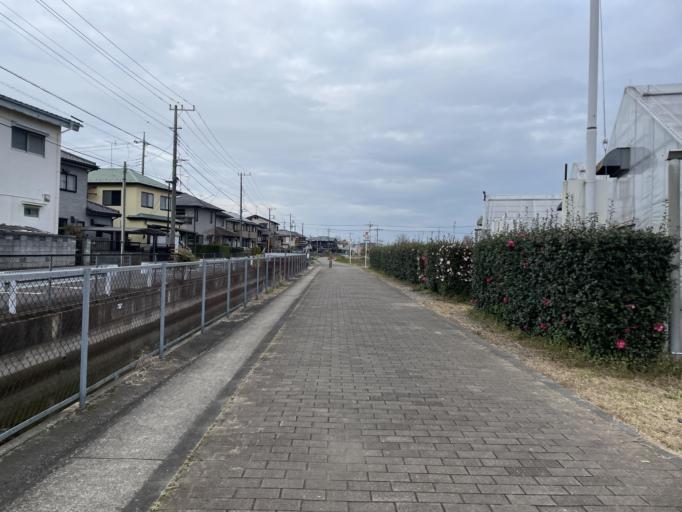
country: JP
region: Saitama
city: Shiraoka
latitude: 36.0226
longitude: 139.6624
